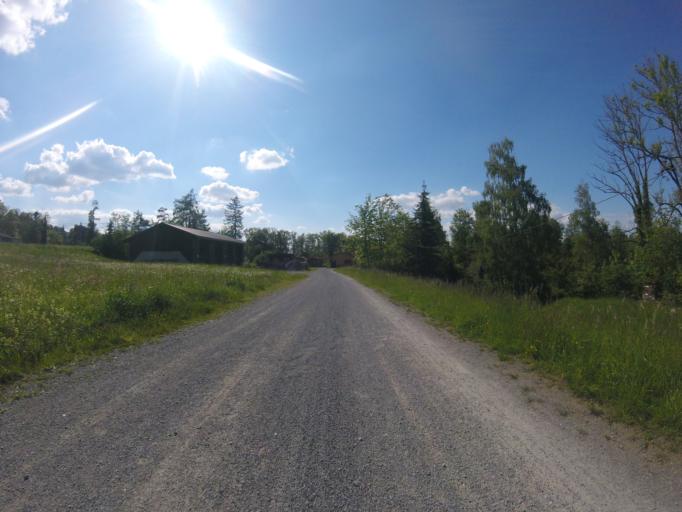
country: CH
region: Saint Gallen
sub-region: Wahlkreis St. Gallen
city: Gossau
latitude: 47.4069
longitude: 9.2209
